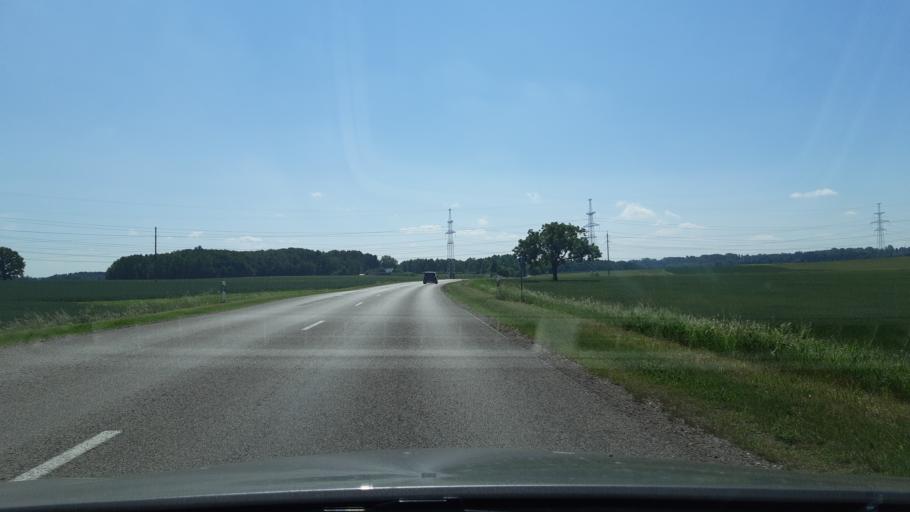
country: LT
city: Ziezmariai
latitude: 54.8208
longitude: 24.2695
